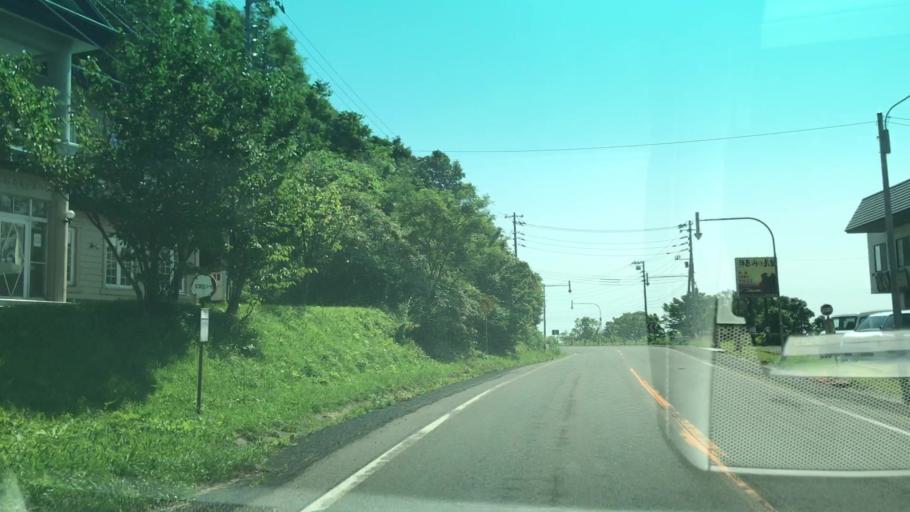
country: JP
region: Hokkaido
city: Iwanai
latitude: 43.1384
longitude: 140.4310
